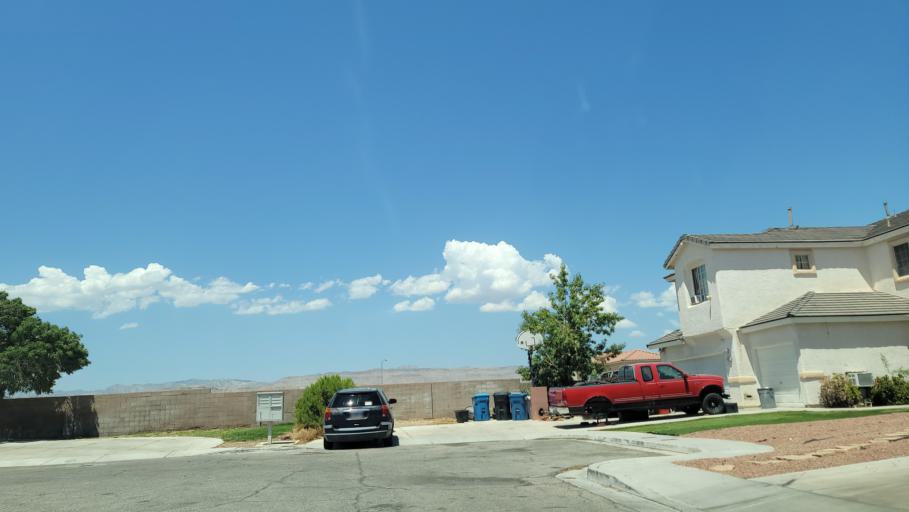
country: US
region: Nevada
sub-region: Clark County
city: Spring Valley
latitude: 36.0838
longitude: -115.2572
